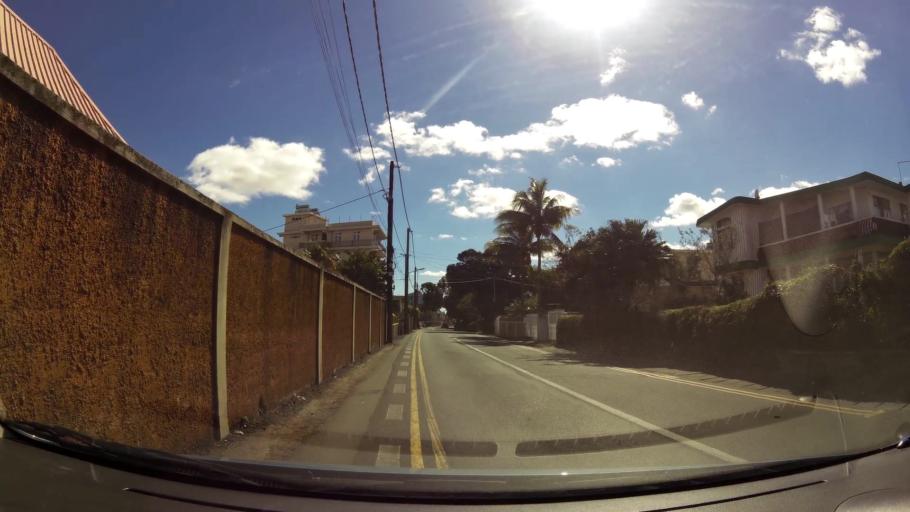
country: MU
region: Plaines Wilhems
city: Vacoas
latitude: -20.2993
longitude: 57.4862
